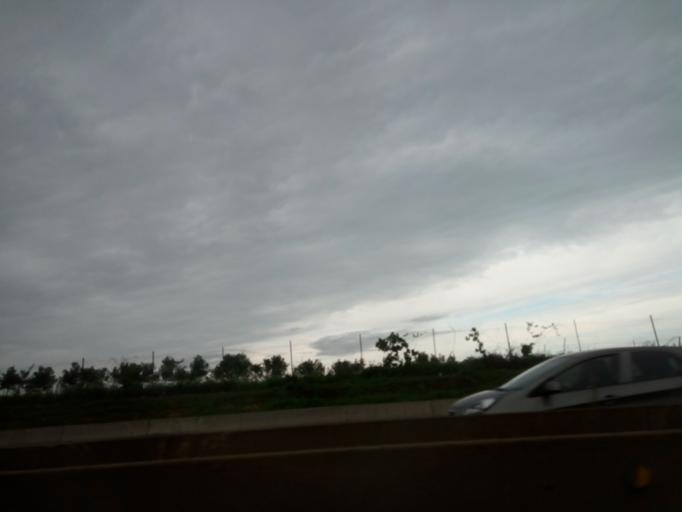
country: DZ
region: Tipaza
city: Cheraga
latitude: 36.7260
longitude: 2.9377
